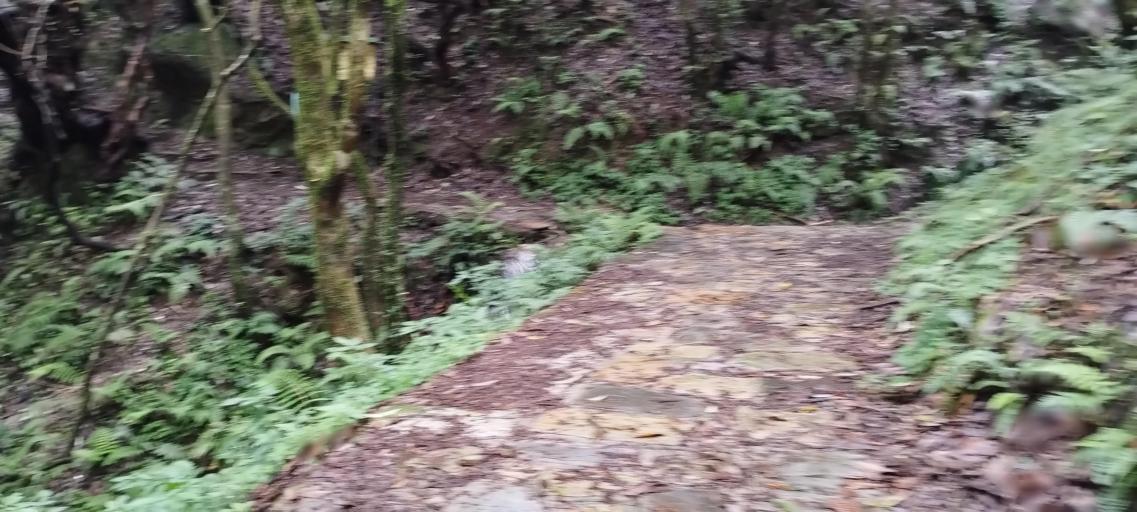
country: NP
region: Central Region
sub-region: Bagmati Zone
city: Kathmandu
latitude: 27.7899
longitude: 85.3842
